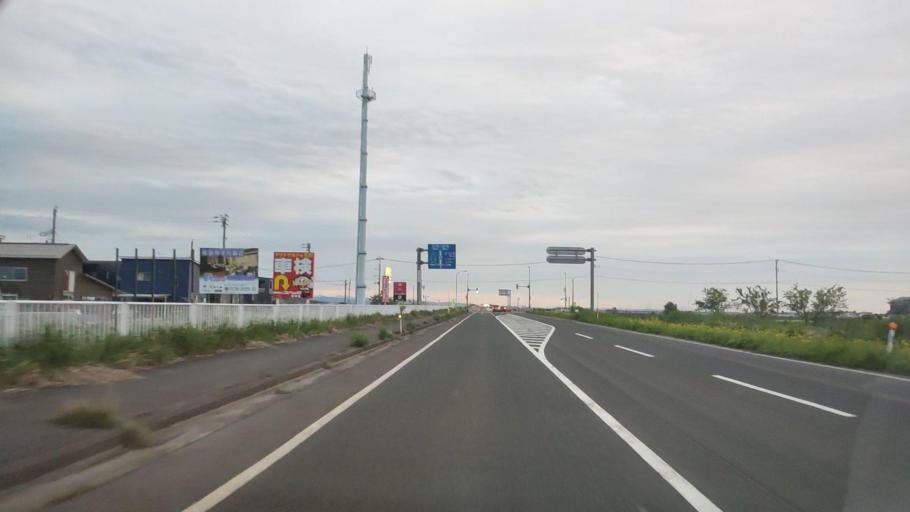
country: JP
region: Niigata
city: Niitsu-honcho
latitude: 37.7525
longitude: 139.0888
